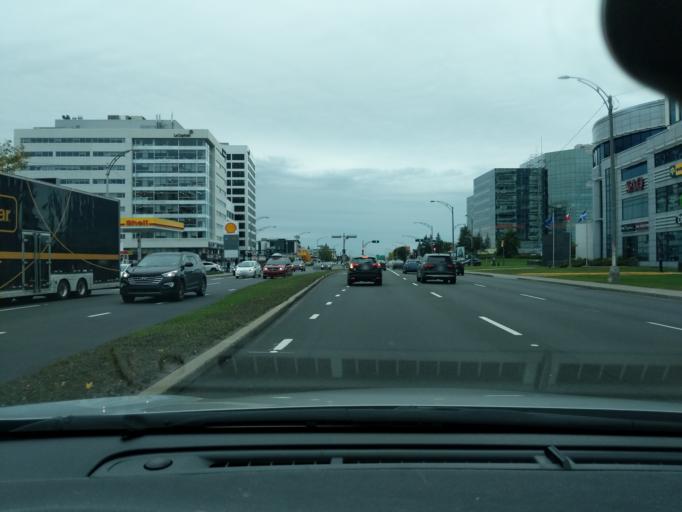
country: CA
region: Quebec
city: L'Ancienne-Lorette
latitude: 46.7677
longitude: -71.2876
